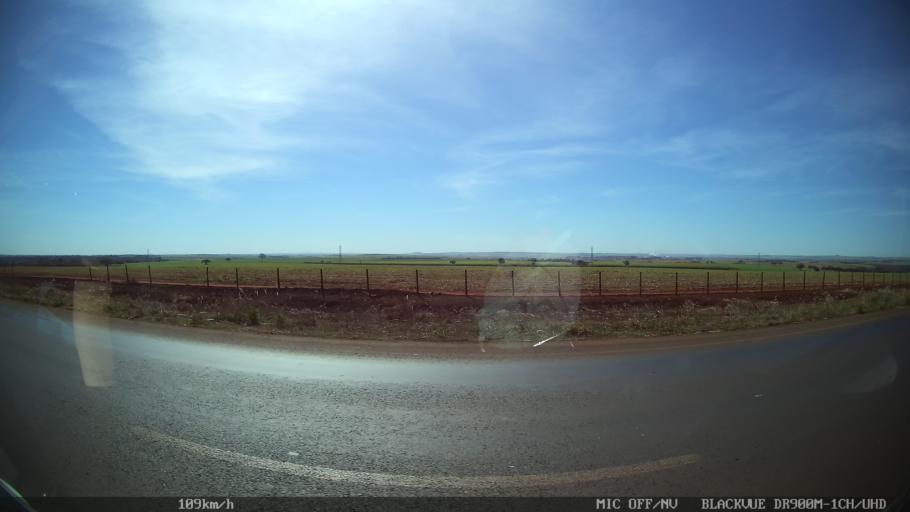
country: BR
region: Sao Paulo
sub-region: Sao Joaquim Da Barra
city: Sao Joaquim da Barra
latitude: -20.5119
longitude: -47.9025
